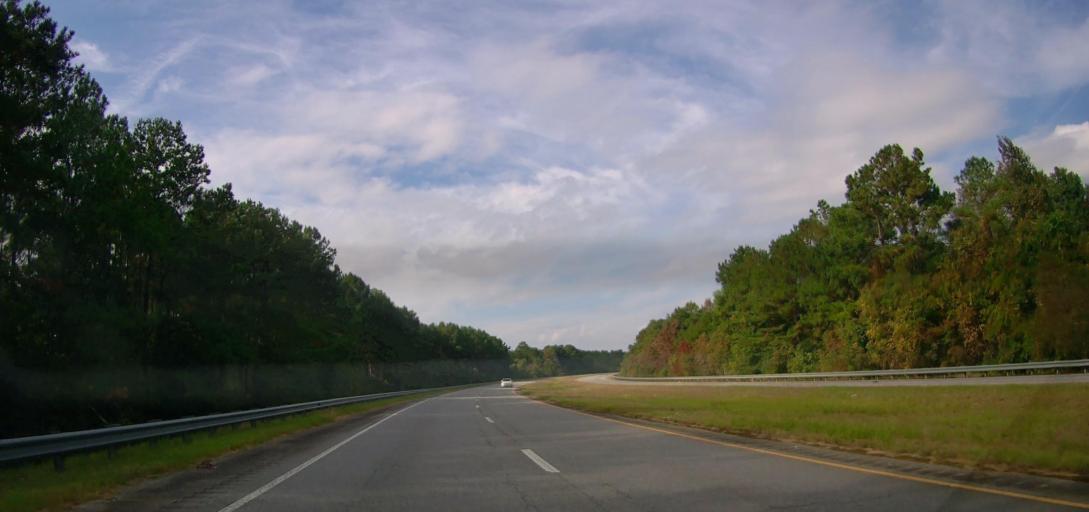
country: US
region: Georgia
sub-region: Thomas County
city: Thomasville
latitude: 30.8204
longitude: -84.0054
